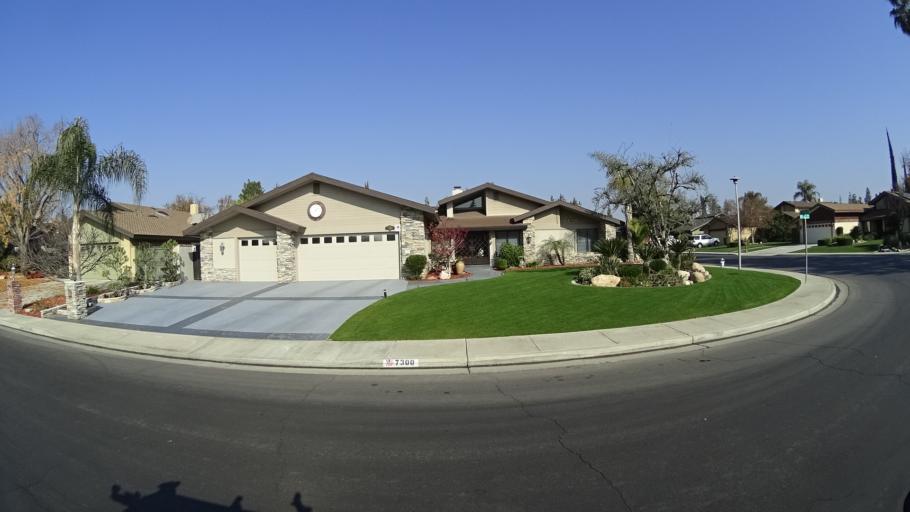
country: US
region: California
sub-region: Kern County
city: Greenacres
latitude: 35.3337
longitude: -119.0824
